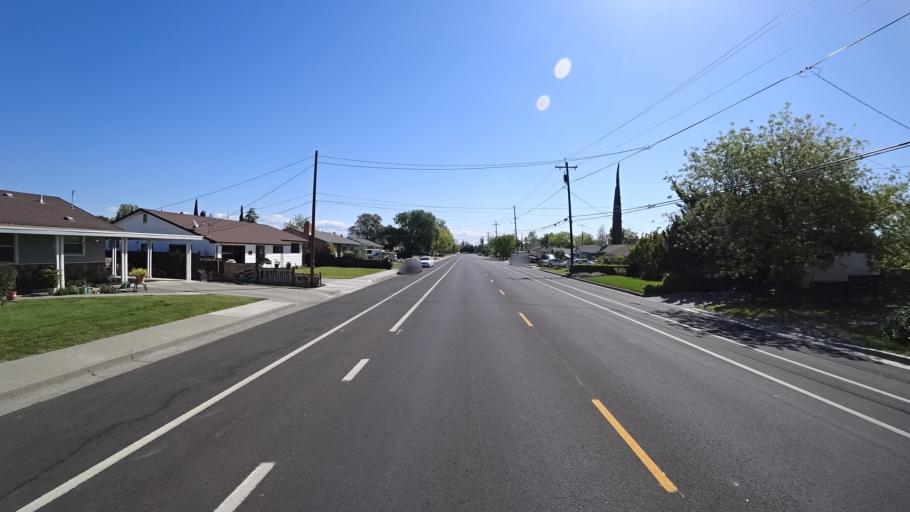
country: US
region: California
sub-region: Glenn County
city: Orland
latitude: 39.7496
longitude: -122.1871
